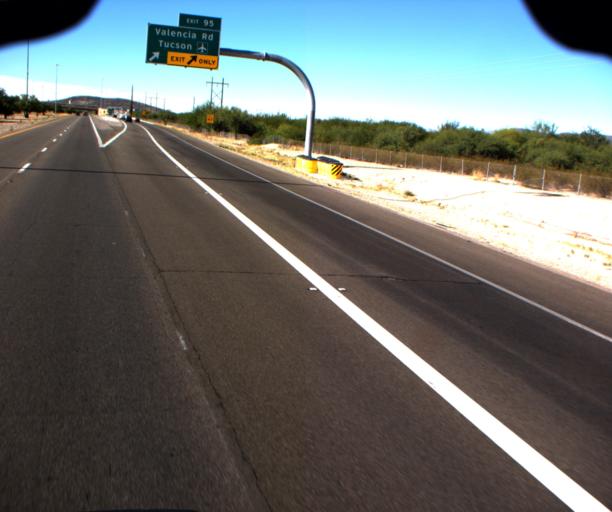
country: US
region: Arizona
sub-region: Pima County
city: Drexel Heights
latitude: 32.1408
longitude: -110.9868
